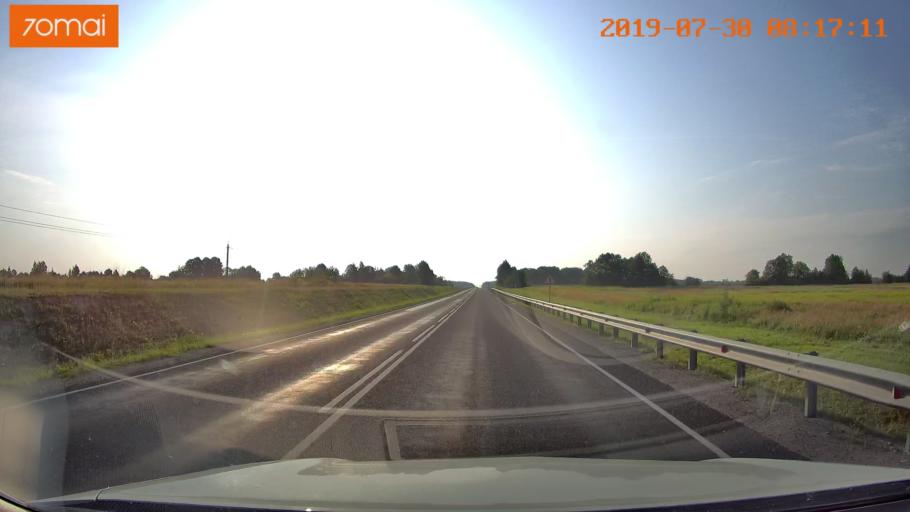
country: RU
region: Kaliningrad
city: Zheleznodorozhnyy
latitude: 54.6373
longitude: 21.4304
